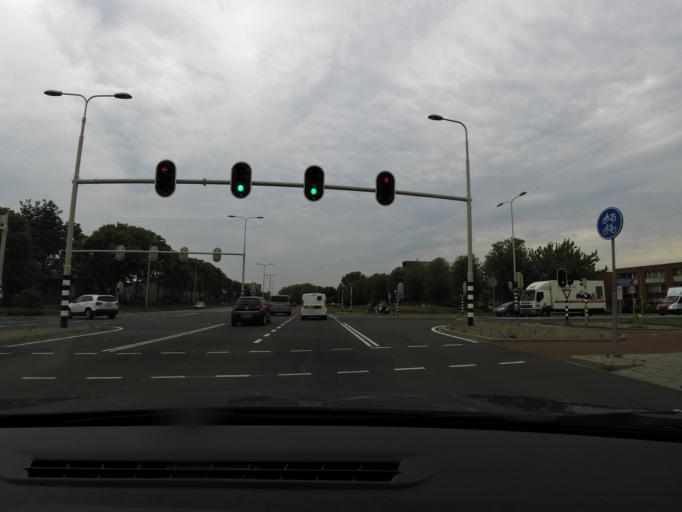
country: NL
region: South Holland
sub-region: Gemeente Spijkenisse
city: Spijkenisse
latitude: 51.8646
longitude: 4.3682
